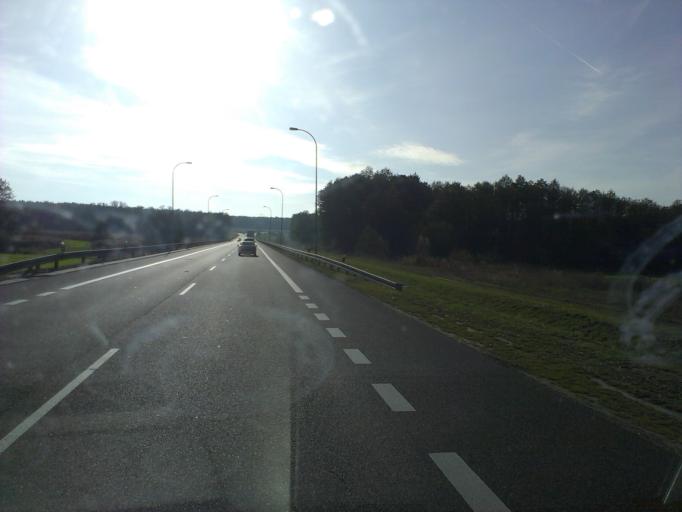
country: PL
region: Lubusz
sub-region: Powiat miedzyrzecki
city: Miedzyrzecz
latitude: 52.4272
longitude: 15.5542
